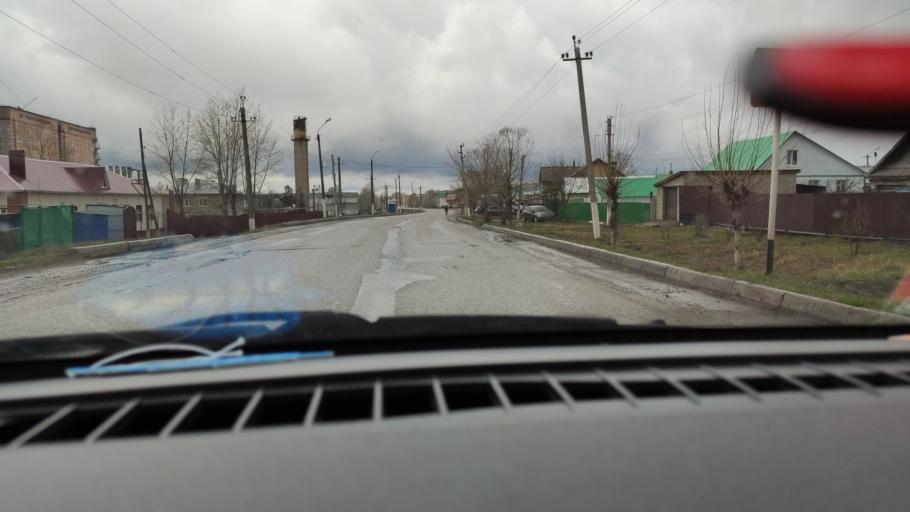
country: RU
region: Tatarstan
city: Nurlat
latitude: 54.4282
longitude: 50.8160
